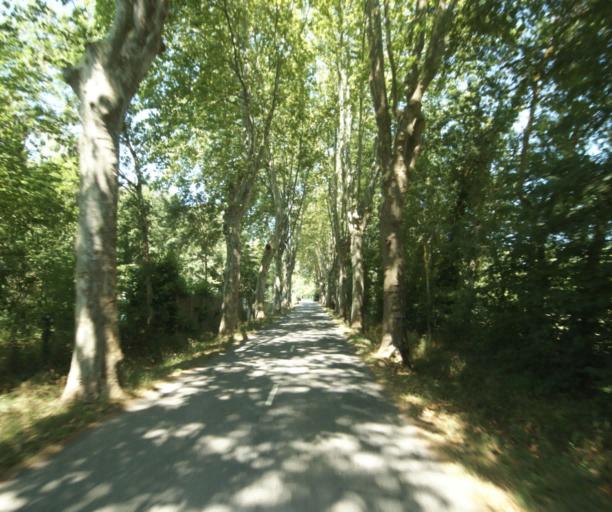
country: FR
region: Midi-Pyrenees
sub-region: Departement de la Haute-Garonne
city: Revel
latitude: 43.4951
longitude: 1.9685
